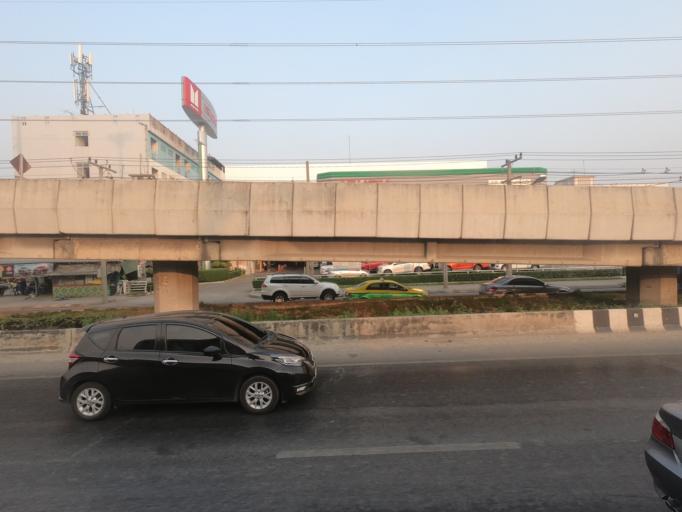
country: TH
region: Pathum Thani
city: Khlong Luang
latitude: 14.0319
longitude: 100.6162
